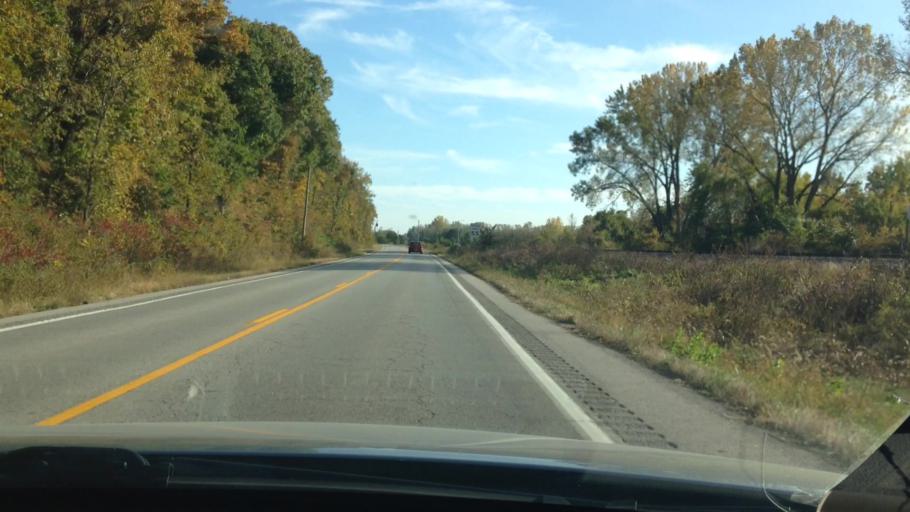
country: US
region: Kansas
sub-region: Leavenworth County
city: Leavenworth
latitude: 39.3188
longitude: -94.8537
